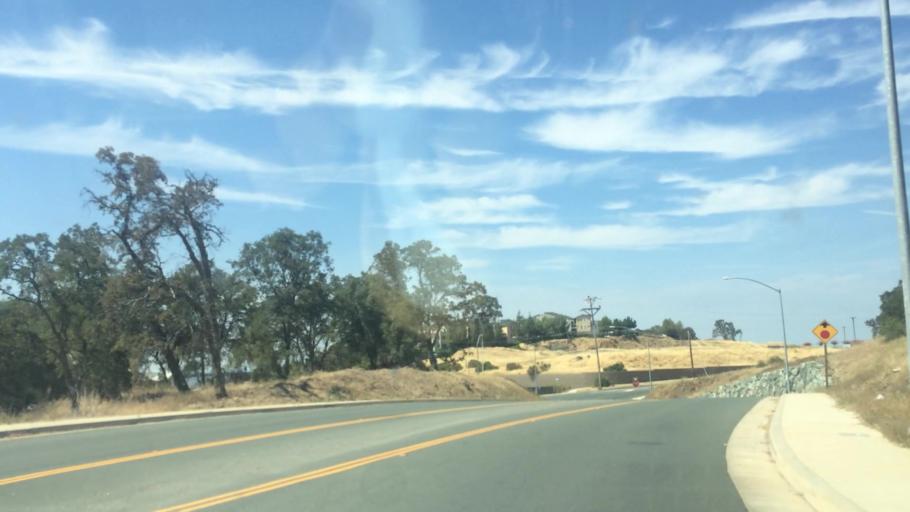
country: US
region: California
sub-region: Amador County
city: Sutter Creek
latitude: 38.3755
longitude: -120.8048
